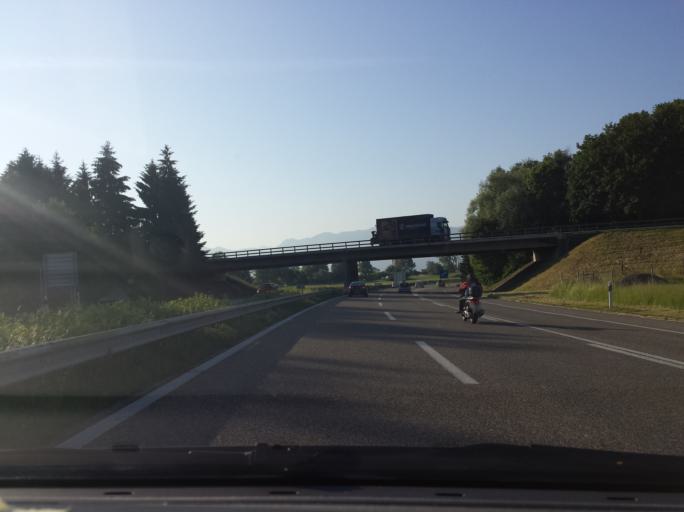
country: AT
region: Vorarlberg
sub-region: Politischer Bezirk Bregenz
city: Hochst
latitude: 47.4535
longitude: 9.6507
